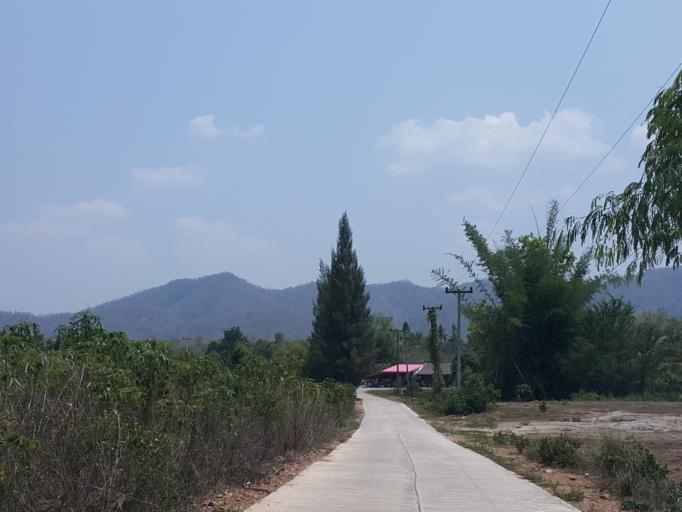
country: TH
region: Kanchanaburi
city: Sai Yok
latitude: 14.1693
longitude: 98.9588
